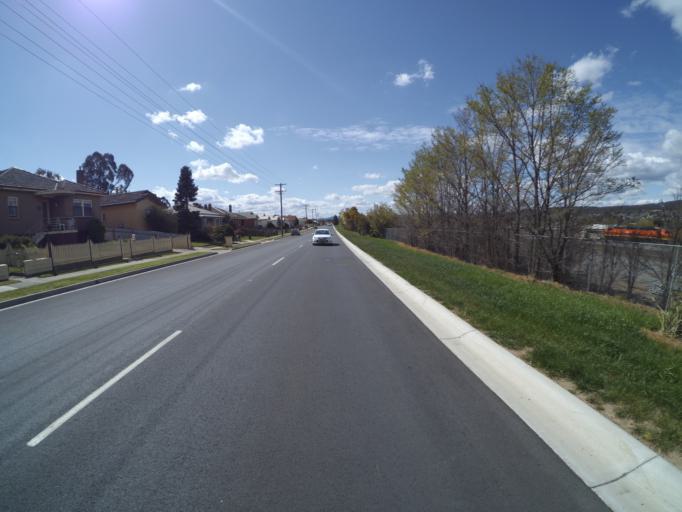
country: AU
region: New South Wales
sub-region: Goulburn Mulwaree
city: Goulburn
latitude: -34.7665
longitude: 149.7123
